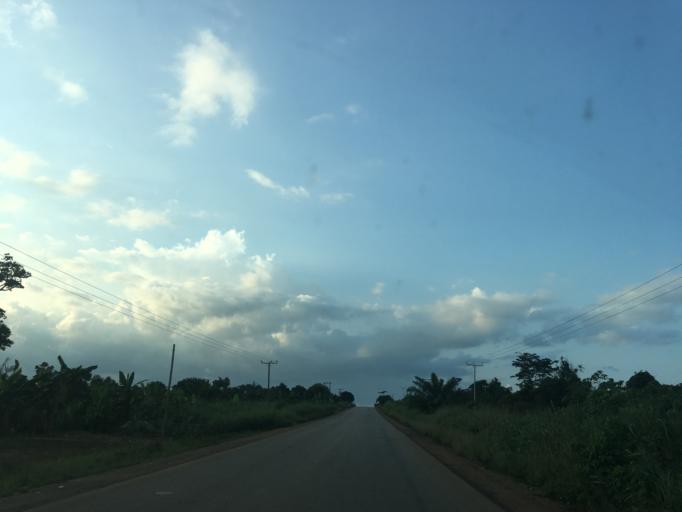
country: GH
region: Western
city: Bibiani
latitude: 6.6406
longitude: -2.4251
